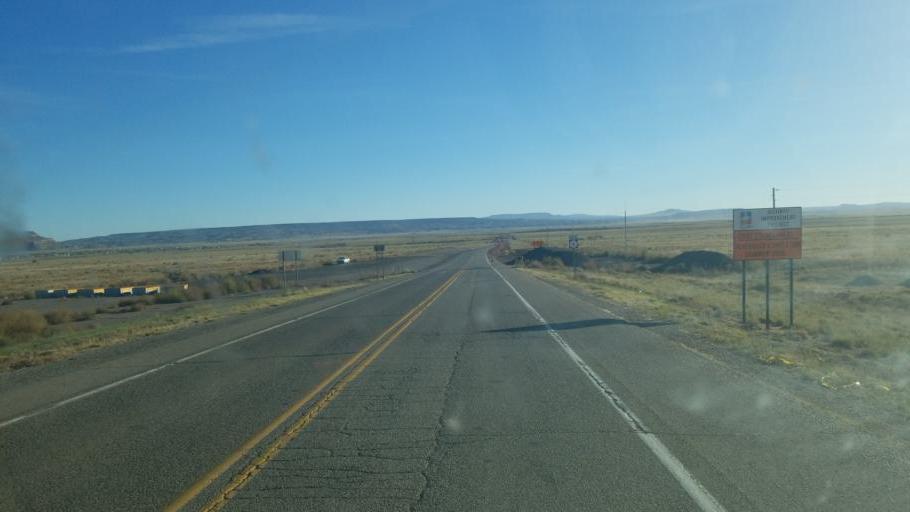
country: US
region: New Mexico
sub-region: Cibola County
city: Laguna
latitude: 34.9822
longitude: -107.1716
